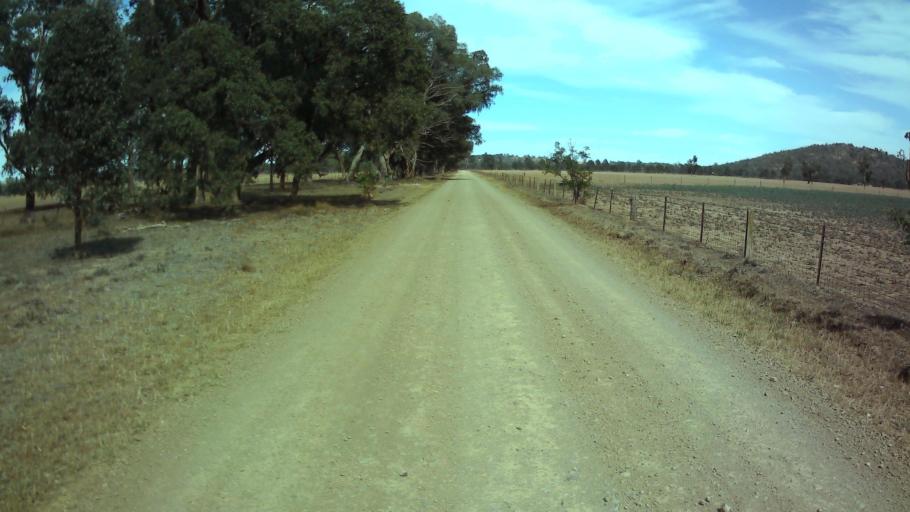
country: AU
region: New South Wales
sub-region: Weddin
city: Grenfell
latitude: -33.6864
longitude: 148.3016
